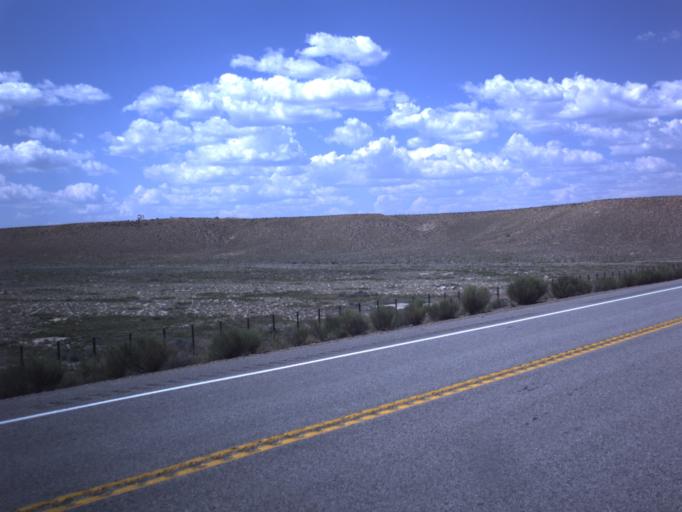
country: US
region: Utah
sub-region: Carbon County
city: Price
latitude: 39.4713
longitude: -110.8560
